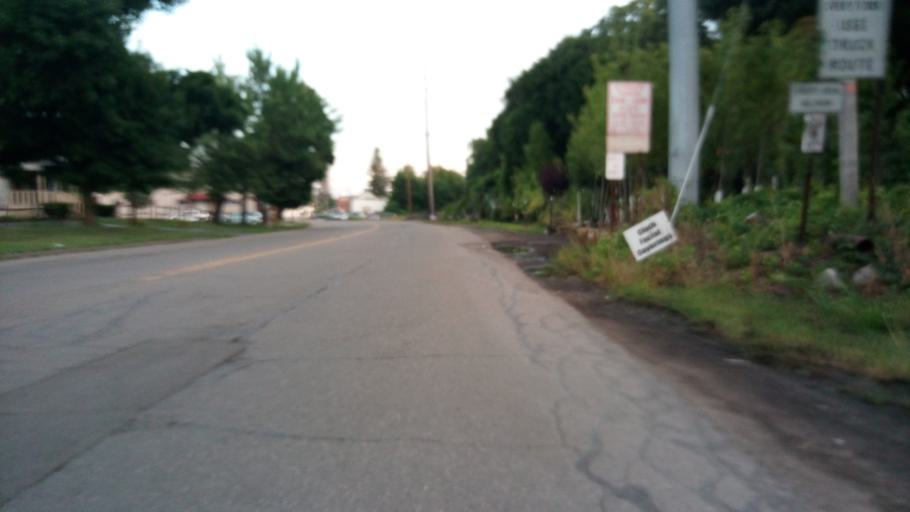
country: US
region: New York
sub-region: Chemung County
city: Elmira Heights
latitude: 42.1330
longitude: -76.8196
